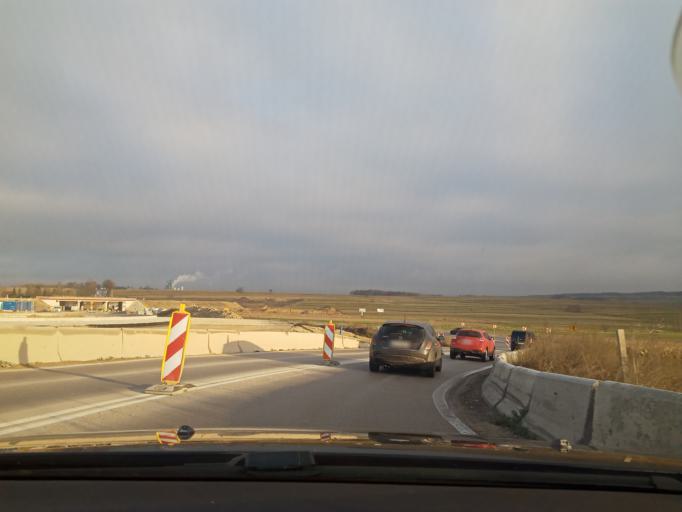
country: PL
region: Lesser Poland Voivodeship
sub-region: Powiat miechowski
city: Miechow
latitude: 50.3125
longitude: 20.0396
